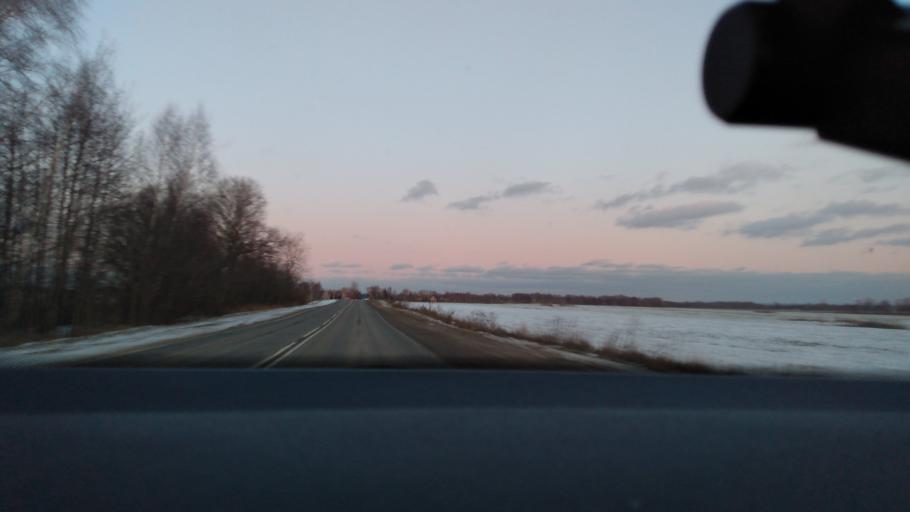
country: RU
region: Moskovskaya
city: Krasnaya Poyma
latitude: 55.1089
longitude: 39.0185
